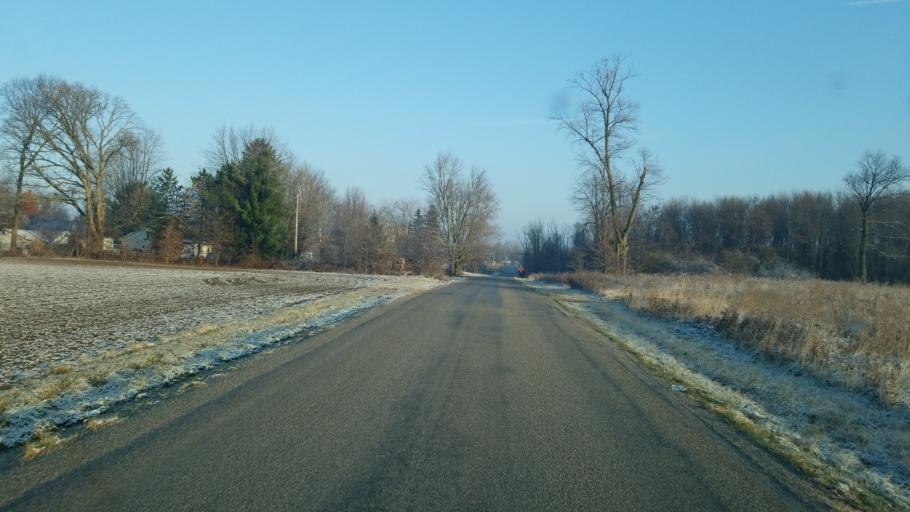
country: US
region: Ohio
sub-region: Crawford County
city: Galion
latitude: 40.6530
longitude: -82.8597
